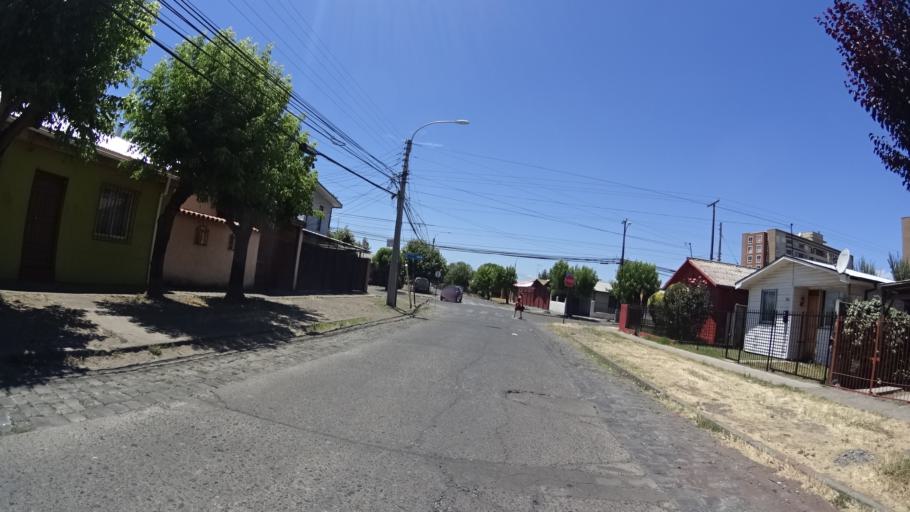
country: CL
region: Biobio
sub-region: Provincia de Nuble
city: Chillan
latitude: -36.6072
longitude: -72.0877
